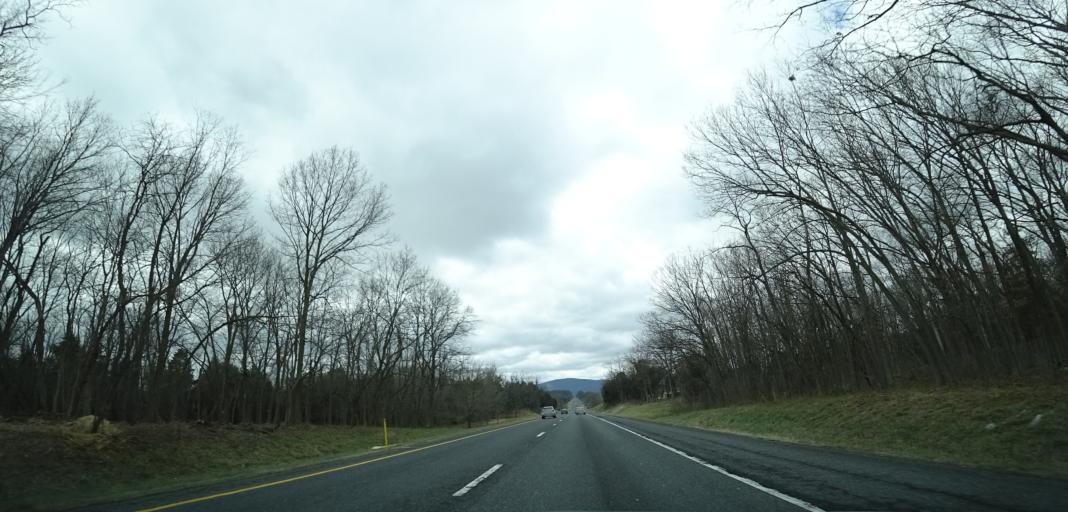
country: US
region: Maryland
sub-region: Washington County
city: Wilson-Conococheague
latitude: 39.6521
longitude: -77.8916
